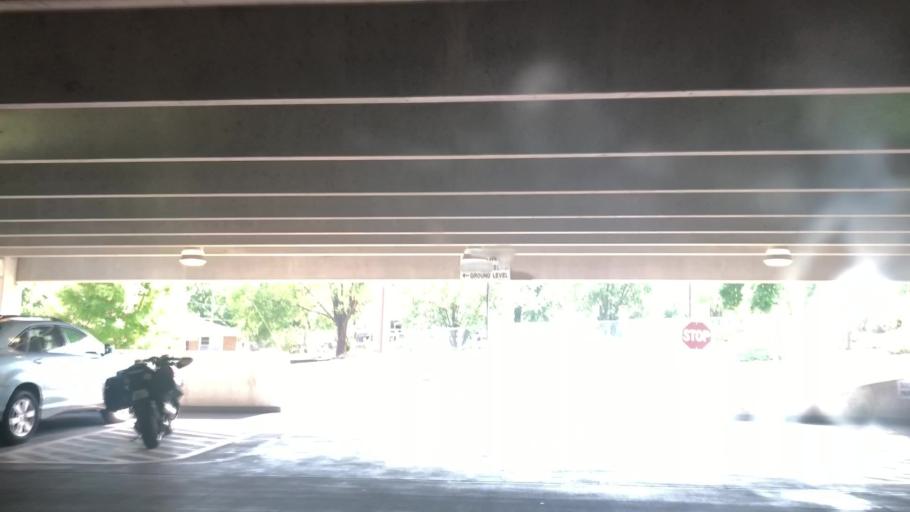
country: US
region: Missouri
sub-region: Taney County
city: Branson
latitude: 36.6501
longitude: -93.2213
